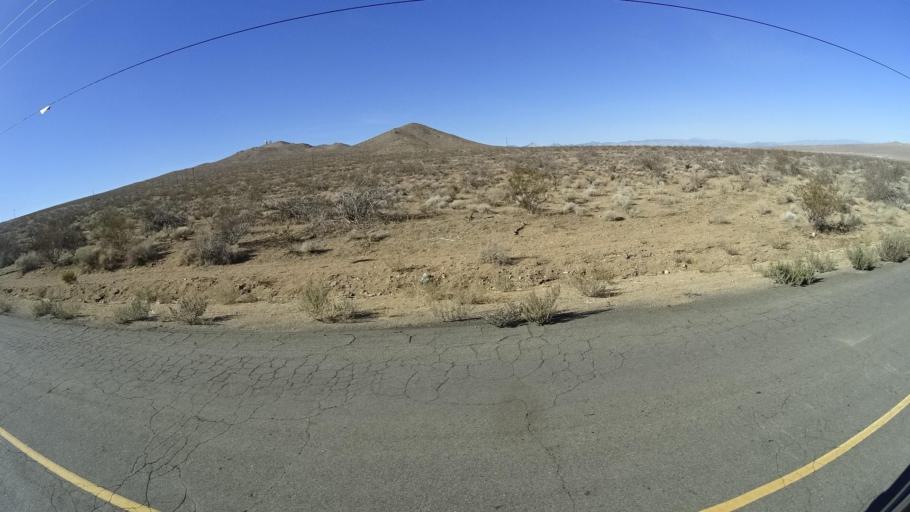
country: US
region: California
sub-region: Kern County
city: Ridgecrest
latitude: 35.4752
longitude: -117.6494
